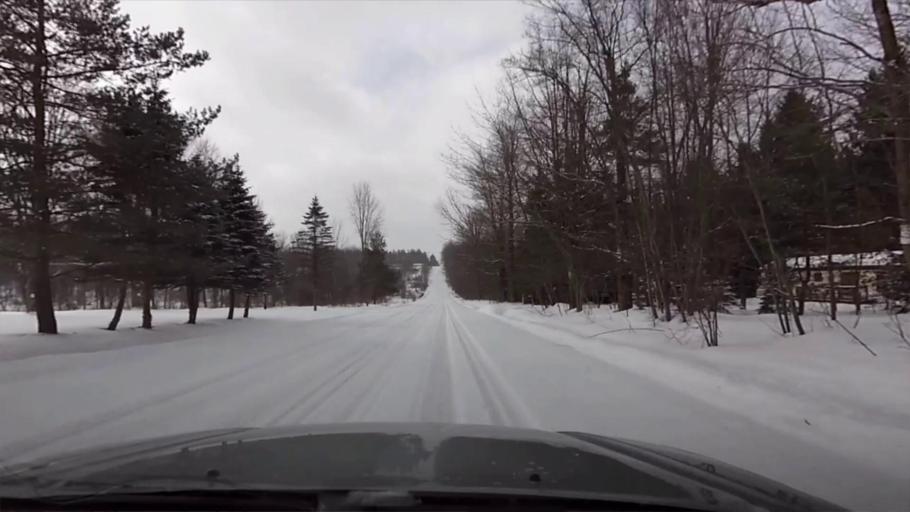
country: US
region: New York
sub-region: Cattaraugus County
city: Franklinville
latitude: 42.3233
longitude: -78.3540
